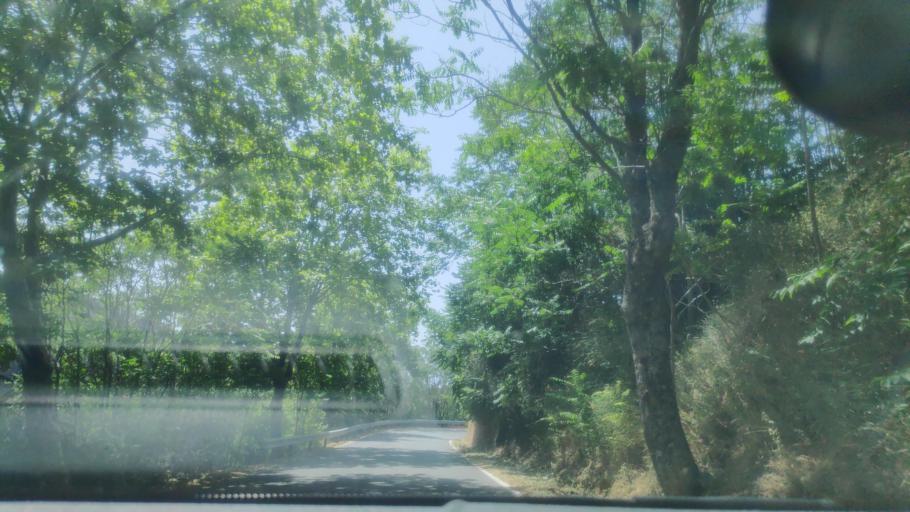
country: ES
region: Andalusia
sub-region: Provincia de Granada
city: Busquistar
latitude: 36.9386
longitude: -3.2904
